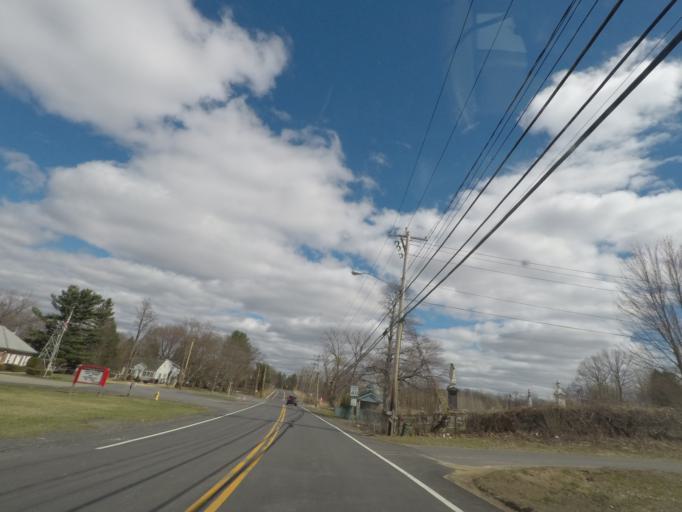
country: US
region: New York
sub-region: Albany County
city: Delmar
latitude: 42.6001
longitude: -73.7888
